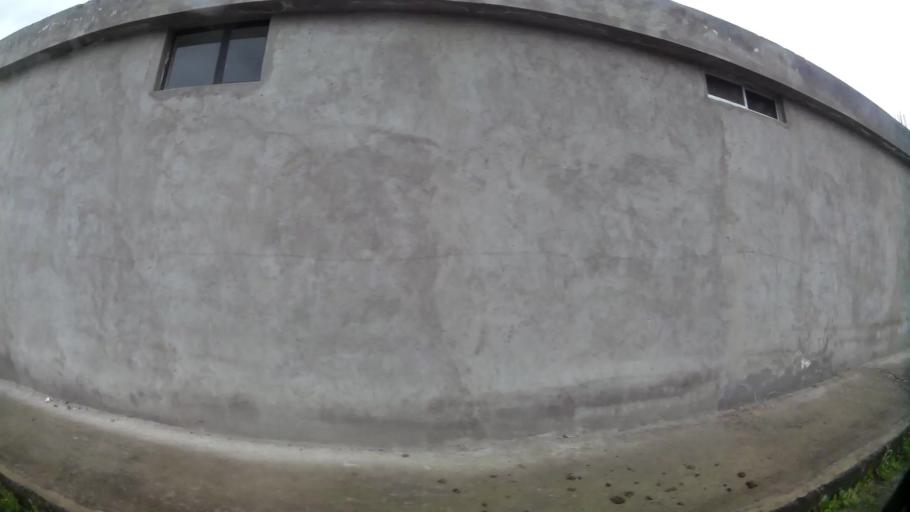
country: EC
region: Pichincha
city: Sangolqui
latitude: -0.3194
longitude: -78.4350
